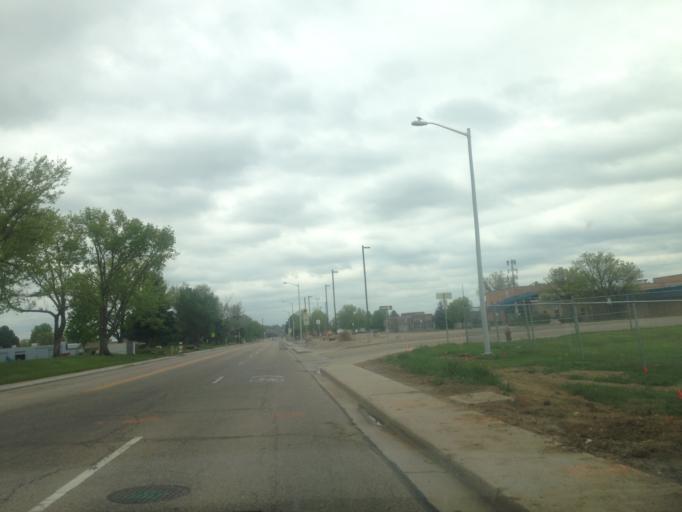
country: US
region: Colorado
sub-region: Boulder County
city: Longmont
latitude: 40.1431
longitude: -105.1215
